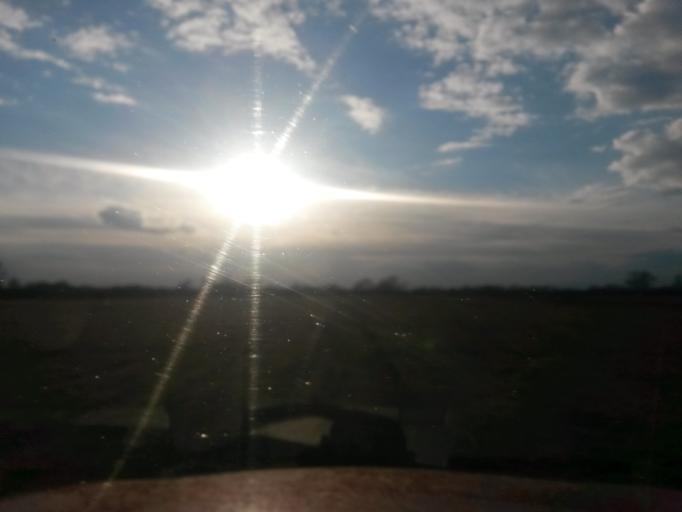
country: SK
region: Kosicky
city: Sobrance
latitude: 48.7035
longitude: 22.0800
